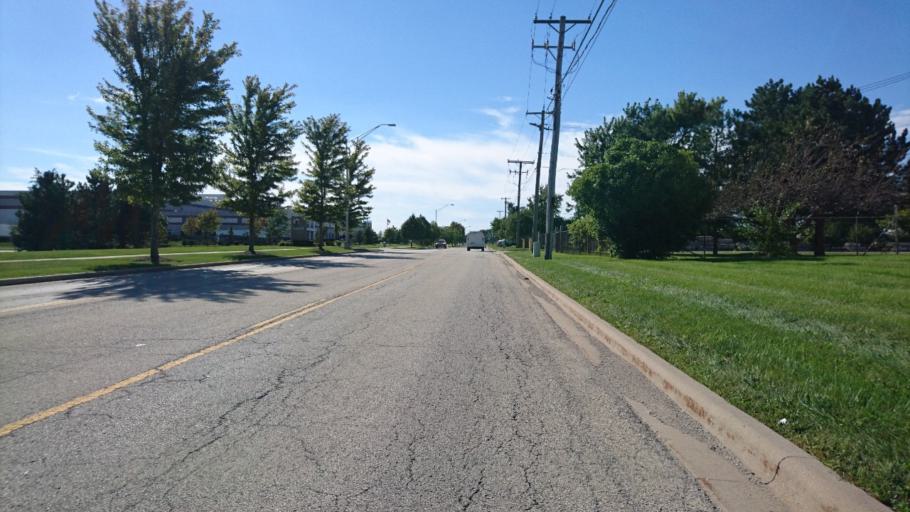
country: US
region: Illinois
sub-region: Will County
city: Ingalls Park
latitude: 41.5113
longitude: -88.0163
